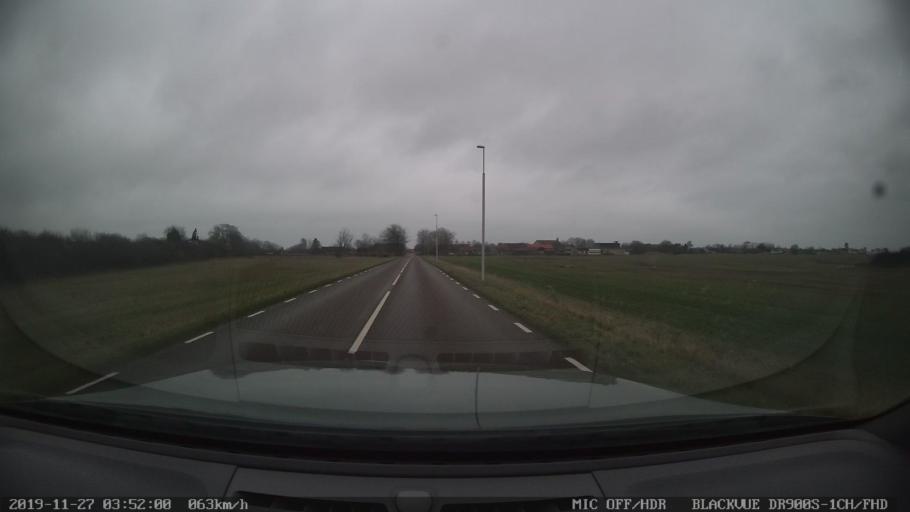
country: SE
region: Skane
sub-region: Hoganas Kommun
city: Hoganas
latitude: 56.2455
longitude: 12.5461
